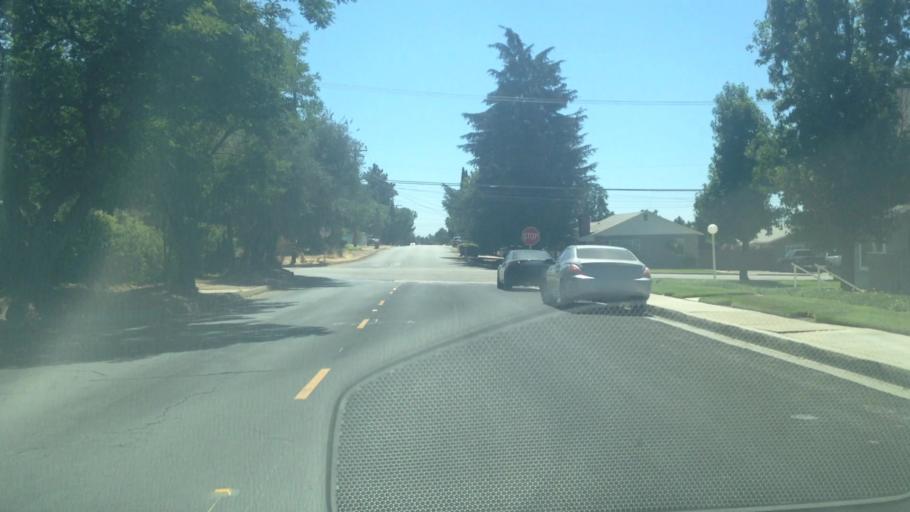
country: US
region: California
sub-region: San Bernardino County
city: Yucaipa
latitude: 34.0272
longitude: -117.0432
